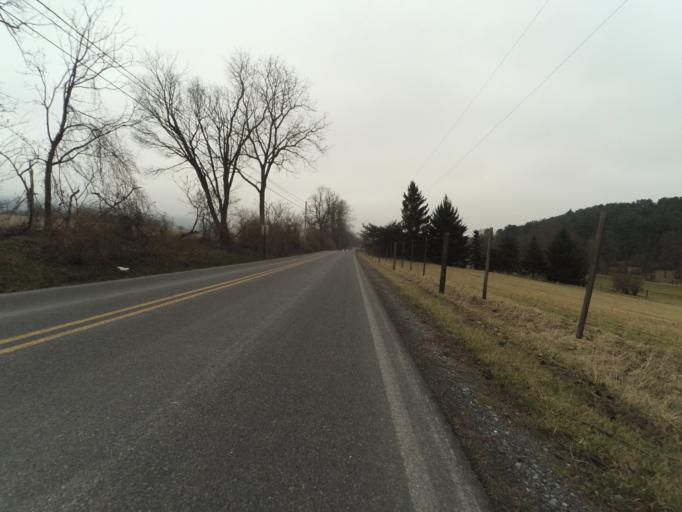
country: US
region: Pennsylvania
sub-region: Centre County
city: Boalsburg
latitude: 40.8032
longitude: -77.7508
